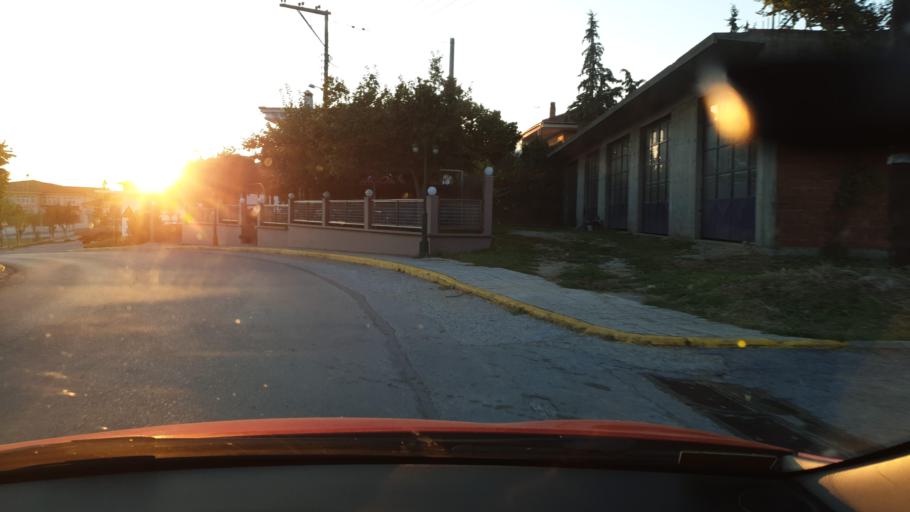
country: GR
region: Central Macedonia
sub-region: Nomos Chalkidikis
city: Galatista
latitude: 40.4682
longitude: 23.2721
